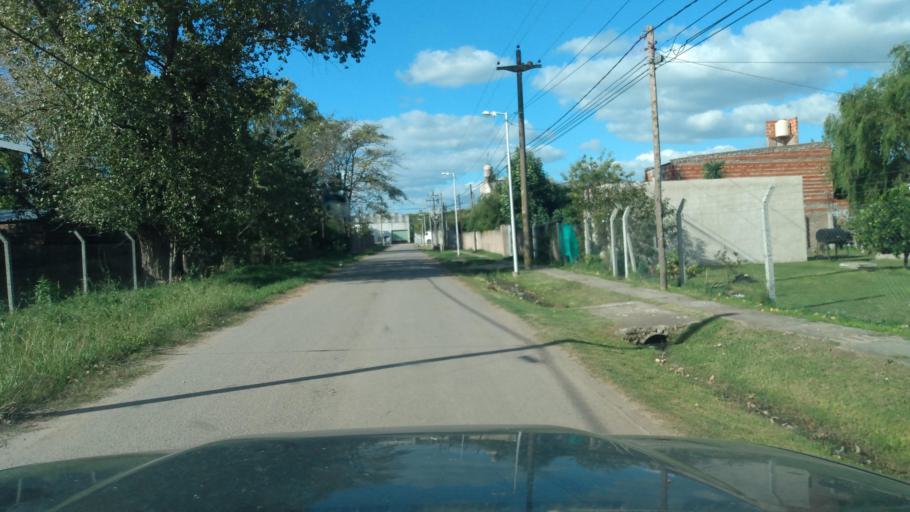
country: AR
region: Buenos Aires
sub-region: Partido de Lujan
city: Lujan
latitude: -34.5820
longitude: -59.0928
